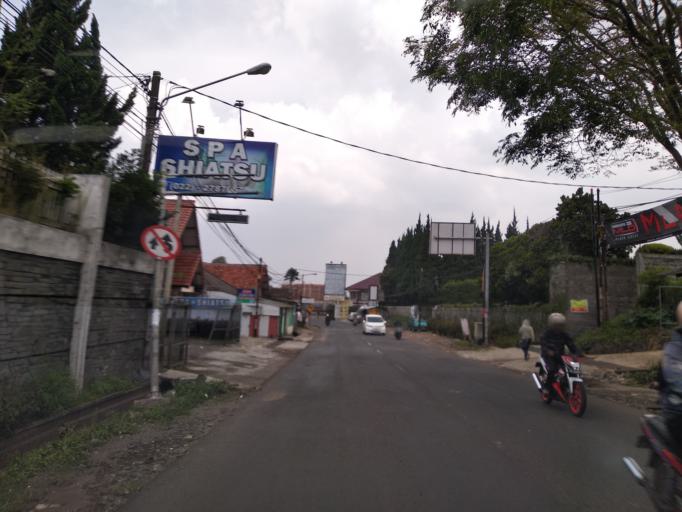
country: ID
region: West Java
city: Lembang
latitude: -6.8210
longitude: 107.6102
